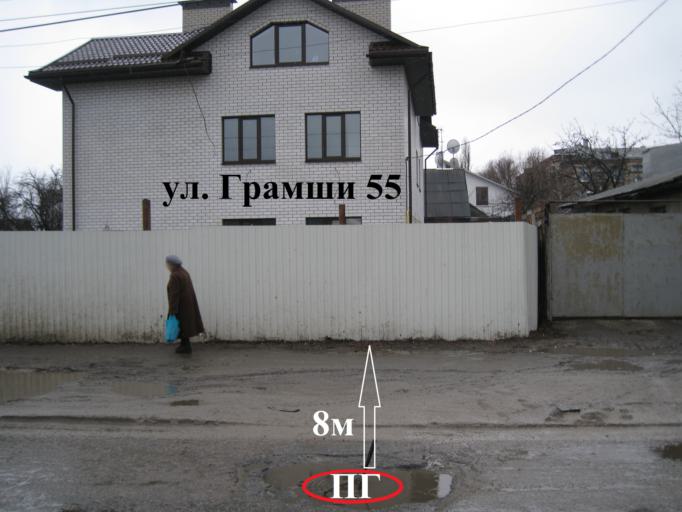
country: RU
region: Voronezj
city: Voronezh
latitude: 51.6341
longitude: 39.1907
